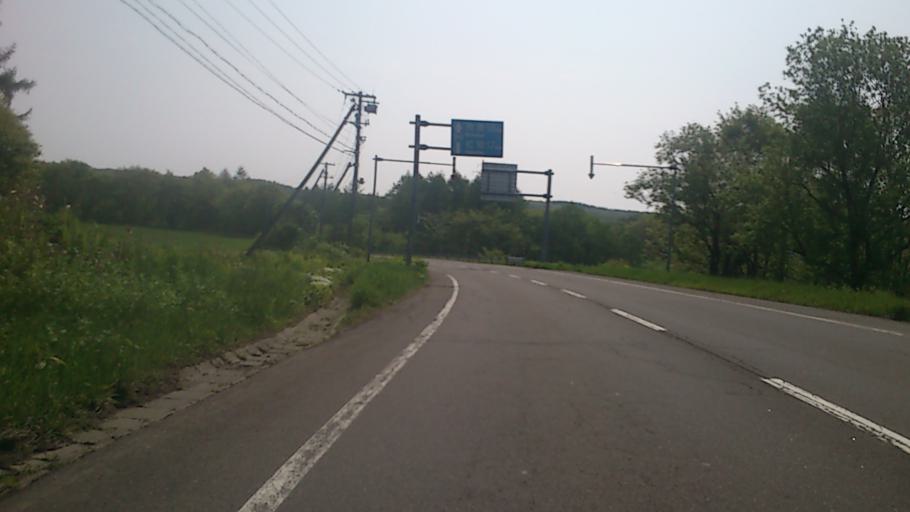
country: JP
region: Hokkaido
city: Bihoro
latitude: 43.4770
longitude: 144.4819
